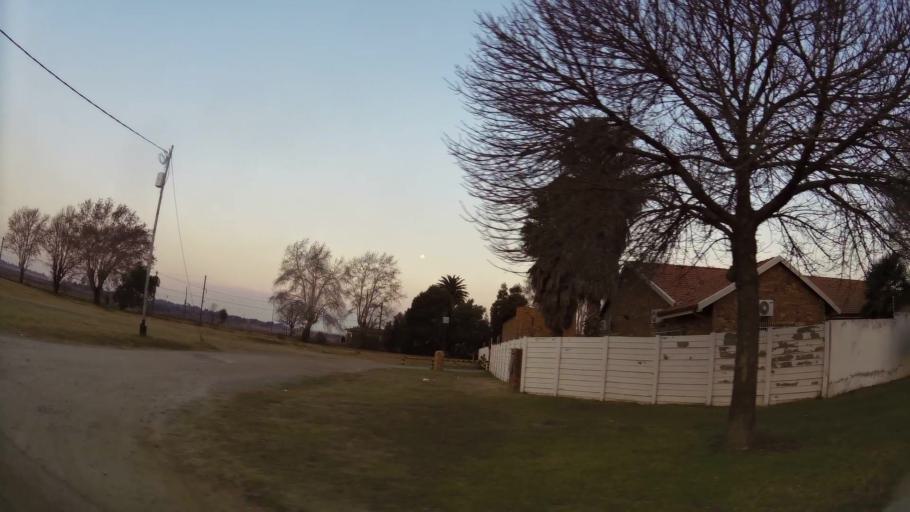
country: ZA
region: Gauteng
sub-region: Ekurhuleni Metropolitan Municipality
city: Nigel
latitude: -26.3491
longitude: 28.4405
